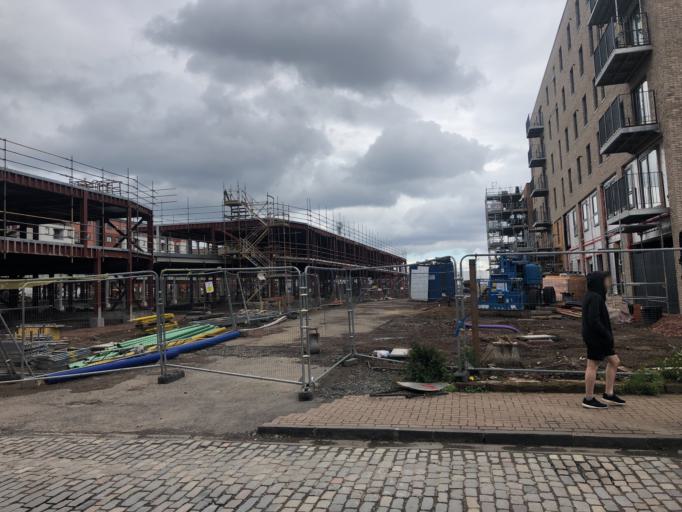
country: GB
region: Scotland
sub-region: West Lothian
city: Seafield
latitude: 55.9732
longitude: -3.1621
